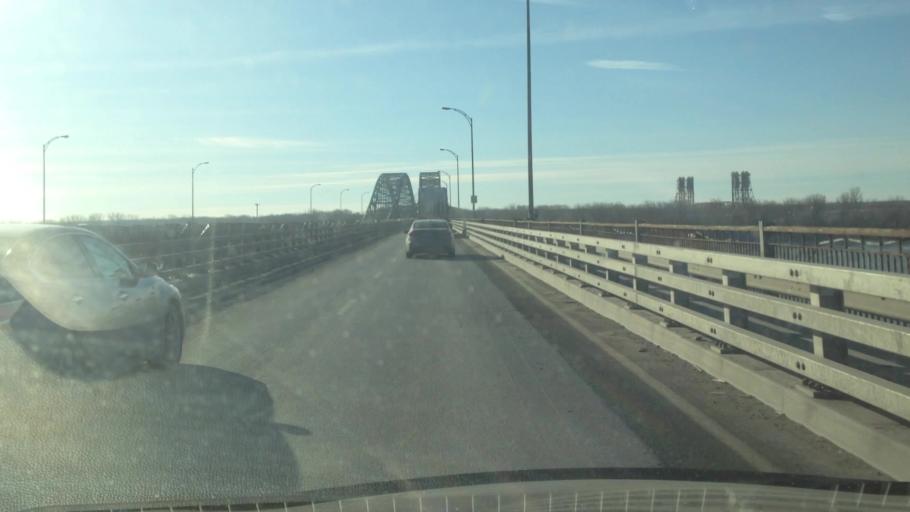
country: CA
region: Quebec
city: Montreal-Ouest
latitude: 45.4193
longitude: -73.6541
